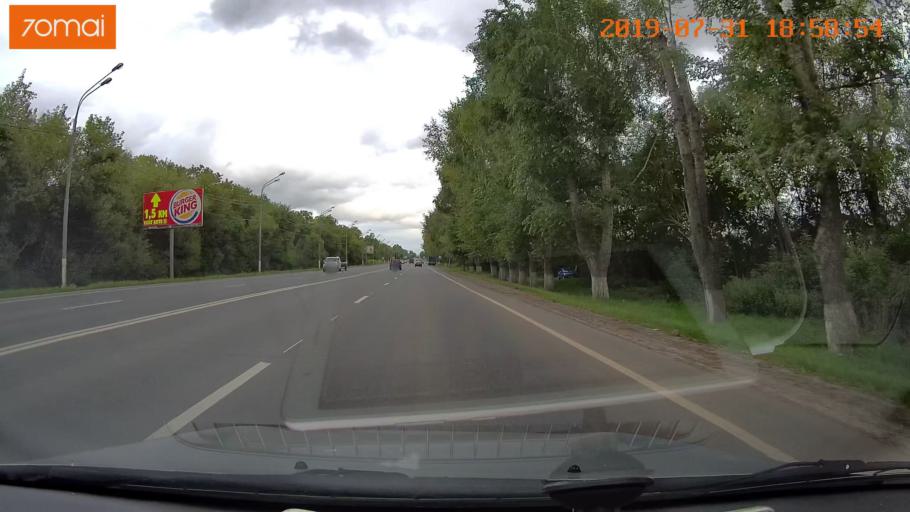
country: RU
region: Moskovskaya
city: Raduzhnyy
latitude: 55.1431
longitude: 38.7099
